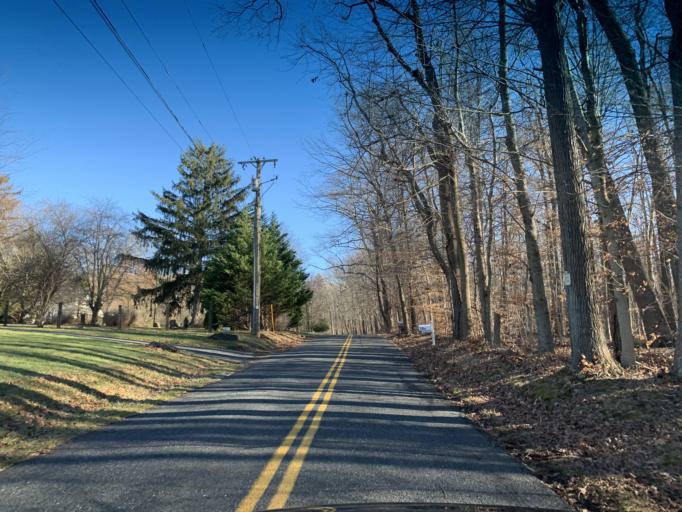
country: US
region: Maryland
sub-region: Harford County
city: Riverside
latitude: 39.5434
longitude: -76.2458
